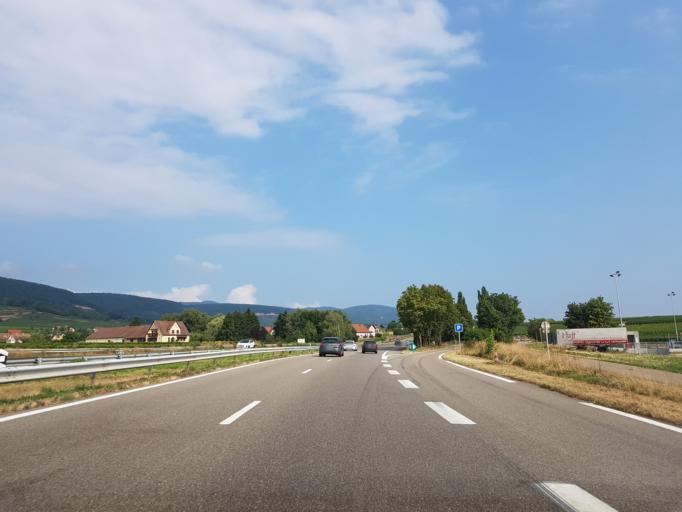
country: FR
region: Alsace
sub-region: Departement du Haut-Rhin
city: Pfaffenheim
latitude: 47.9764
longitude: 7.2954
